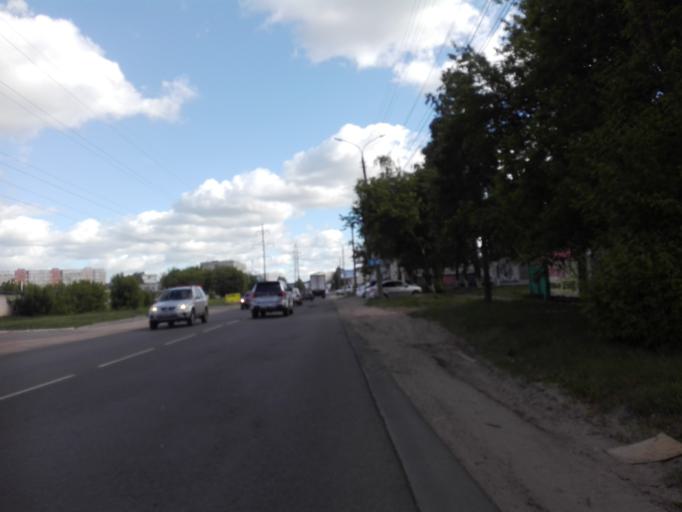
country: RU
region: Orjol
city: Orel
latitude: 52.9419
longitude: 36.0321
